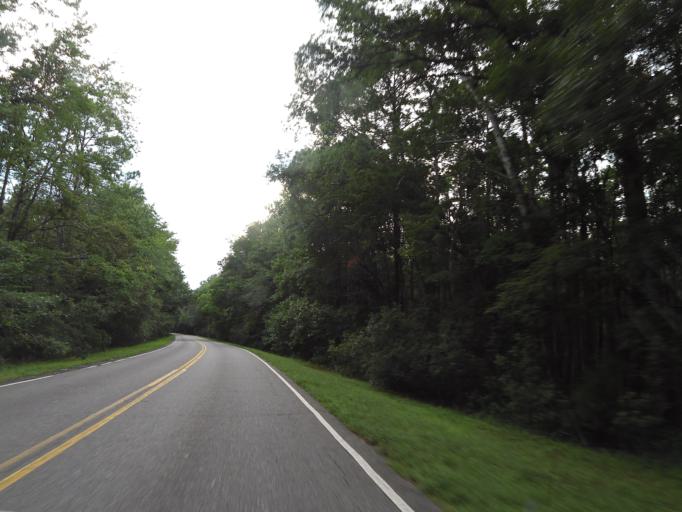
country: US
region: Florida
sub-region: Duval County
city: Jacksonville
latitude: 30.3430
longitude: -81.7776
